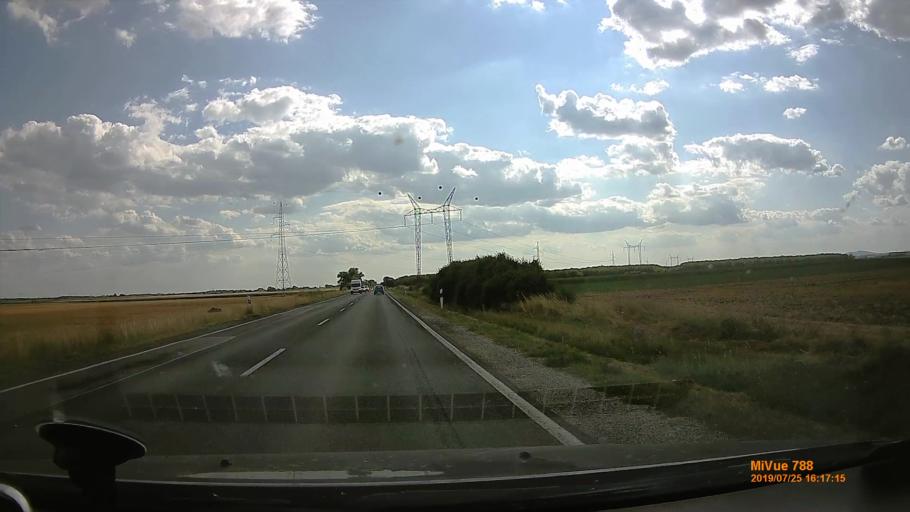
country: HU
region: Heves
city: Kal
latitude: 47.7711
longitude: 20.2783
